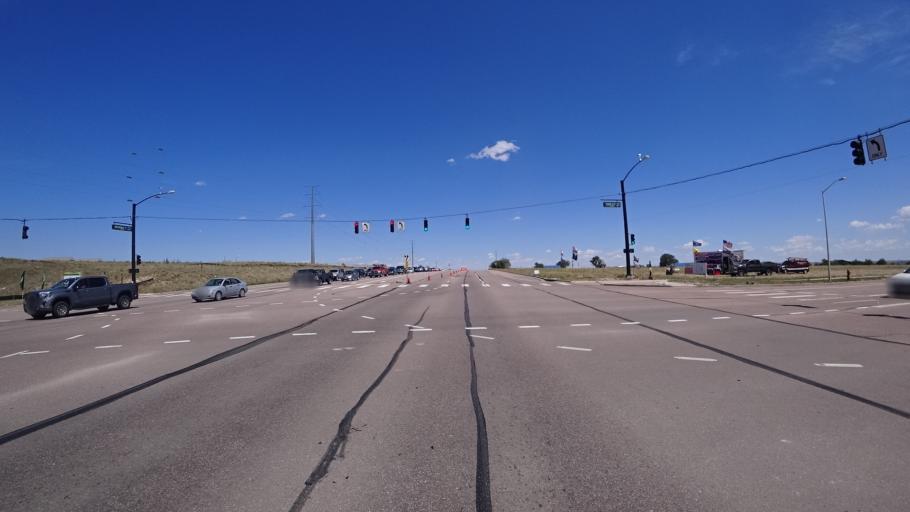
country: US
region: Colorado
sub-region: El Paso County
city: Black Forest
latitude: 38.9405
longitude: -104.7113
